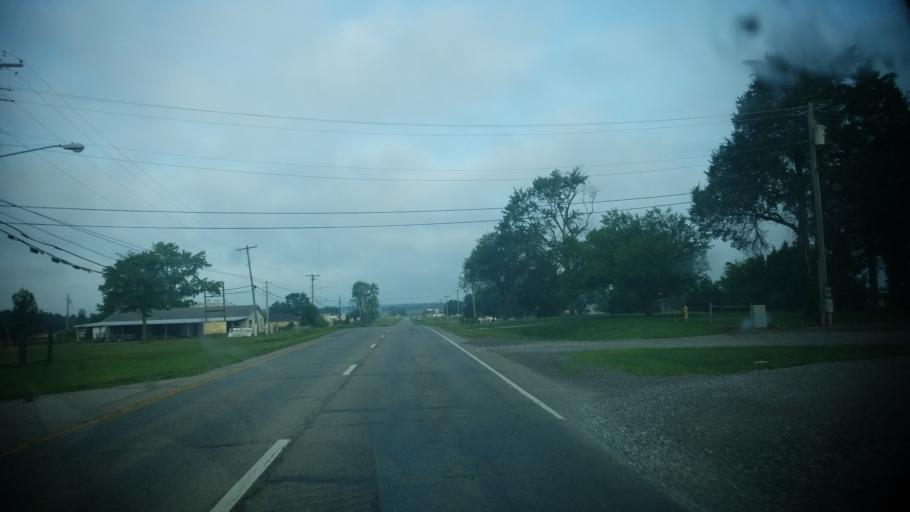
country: US
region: Illinois
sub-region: Wayne County
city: Fairfield
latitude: 38.3797
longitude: -88.3867
